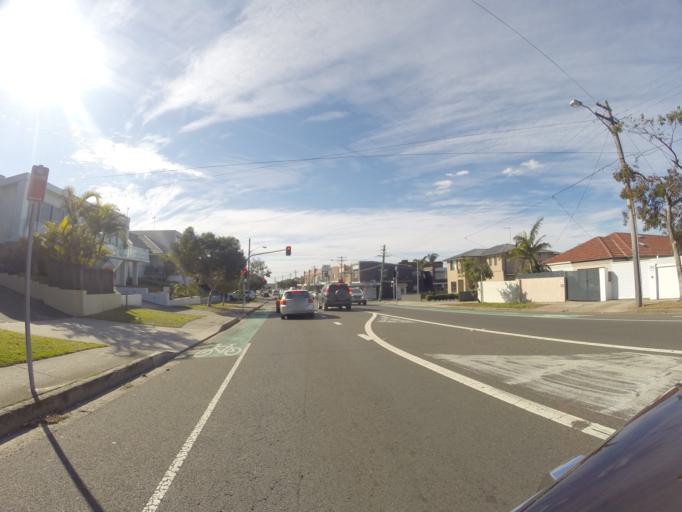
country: AU
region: New South Wales
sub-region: Randwick
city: South Coogee
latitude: -33.9394
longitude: 151.2567
